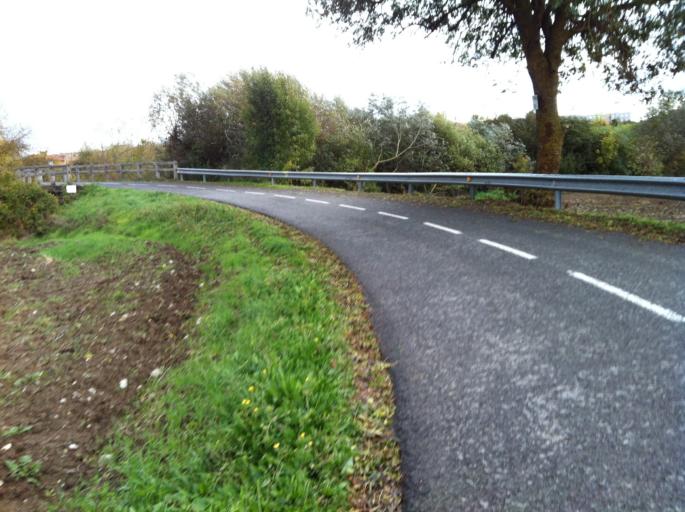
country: ES
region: Basque Country
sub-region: Provincia de Alava
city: Gasteiz / Vitoria
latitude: 42.8727
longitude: -2.6965
